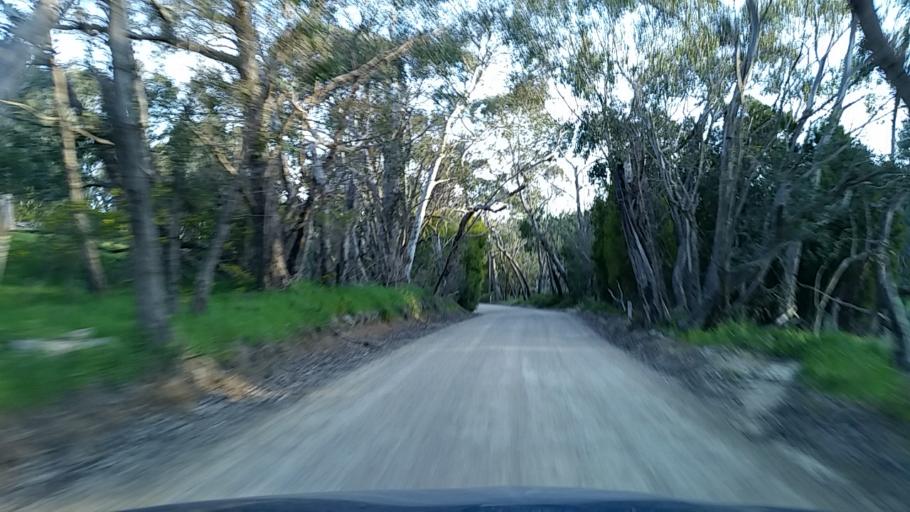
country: AU
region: South Australia
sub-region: Mount Barker
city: Meadows
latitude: -35.2698
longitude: 138.7019
